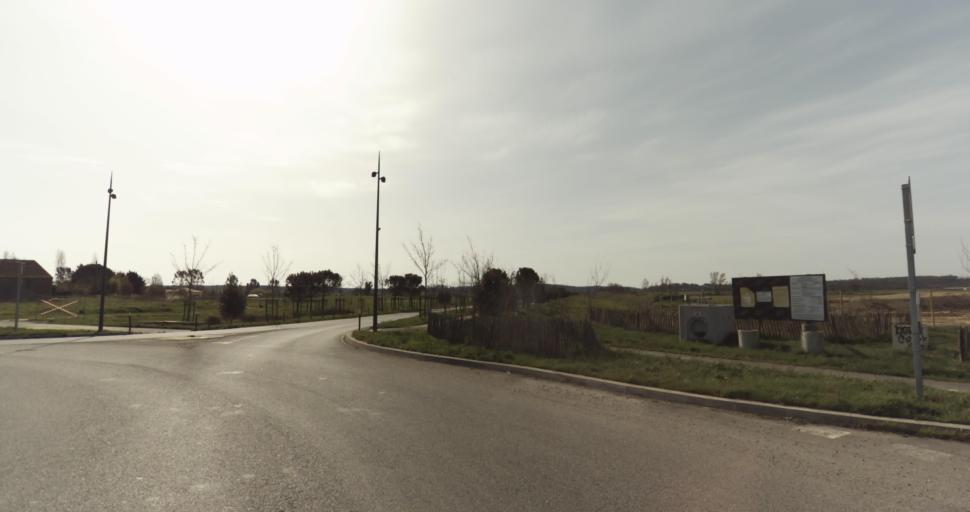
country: FR
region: Midi-Pyrenees
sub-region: Departement de la Haute-Garonne
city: Buzet-sur-Tarn
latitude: 43.7634
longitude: 1.6572
